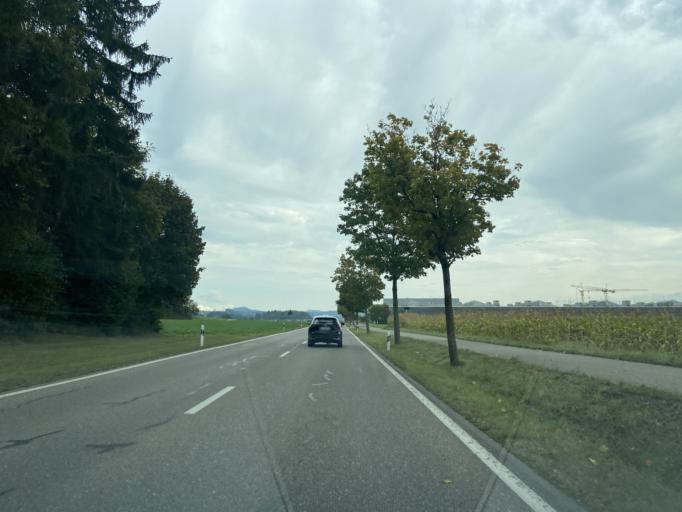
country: CH
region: Zurich
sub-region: Bezirk Pfaeffikon
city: Illnau / Unter-Illnau
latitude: 47.3976
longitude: 8.7355
